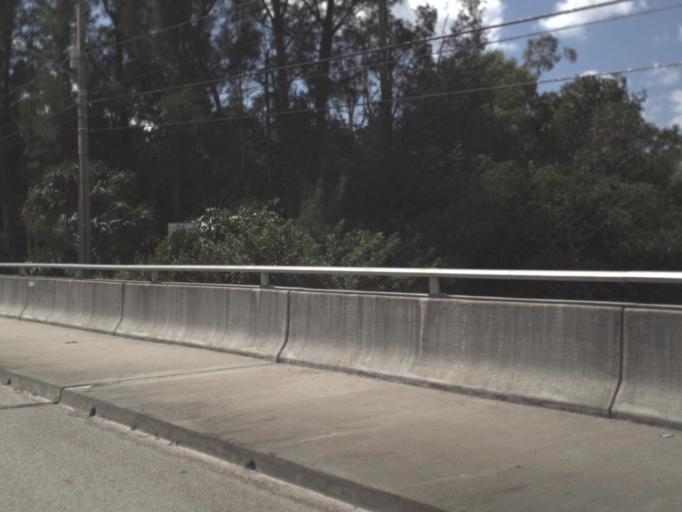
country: US
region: Florida
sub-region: Collier County
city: Naples Park
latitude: 26.2826
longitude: -81.8019
